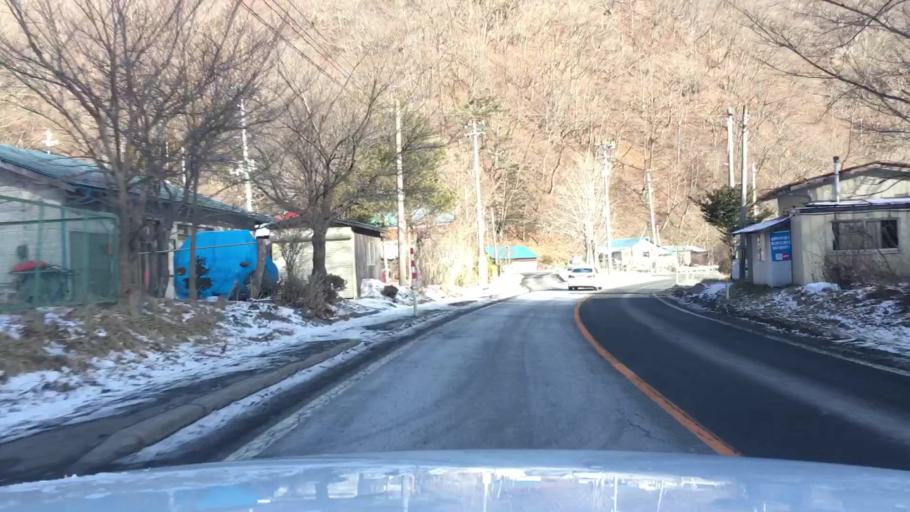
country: JP
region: Iwate
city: Tono
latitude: 39.6260
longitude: 141.5138
